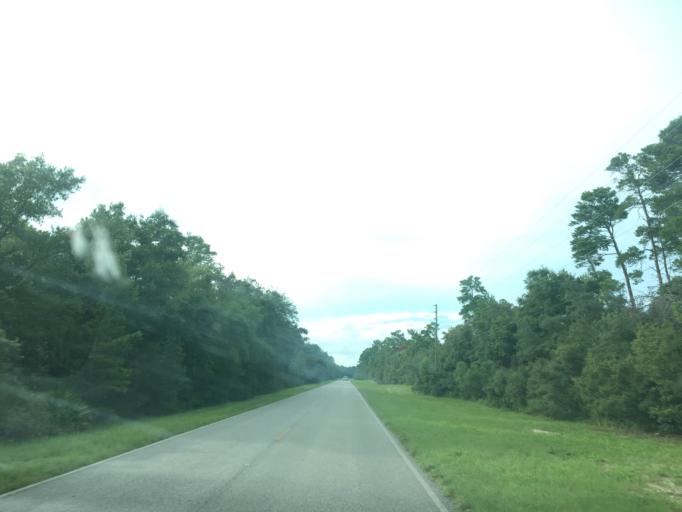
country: US
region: Florida
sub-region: Wakulla County
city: Crawfordville
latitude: 29.9210
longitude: -84.3724
